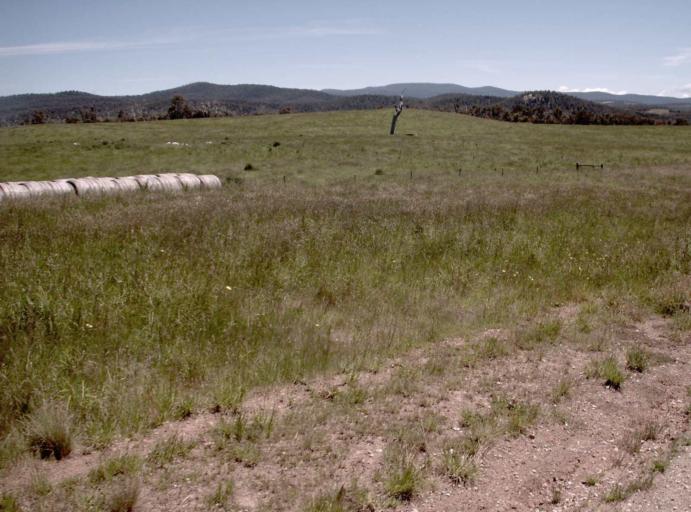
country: AU
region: New South Wales
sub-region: Snowy River
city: Jindabyne
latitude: -37.0879
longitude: 148.2573
